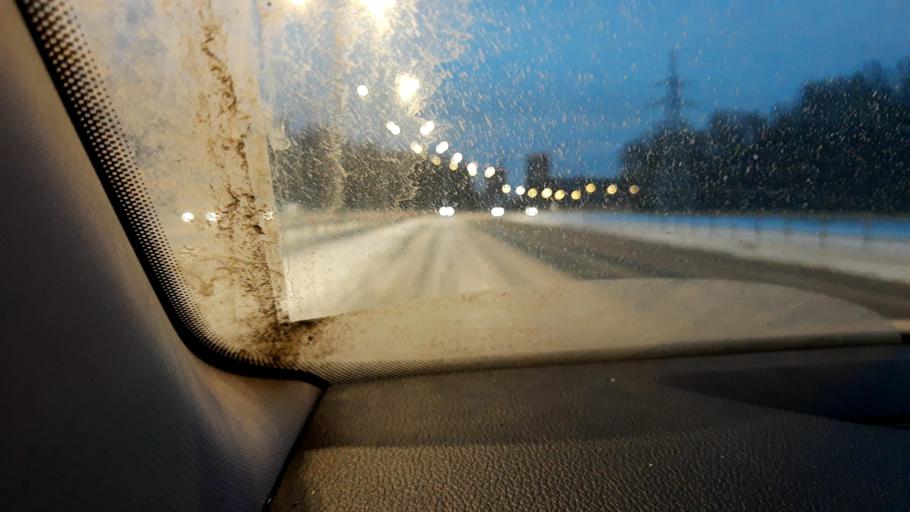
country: RU
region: Moskovskaya
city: Kommunarka
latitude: 55.5864
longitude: 37.4818
